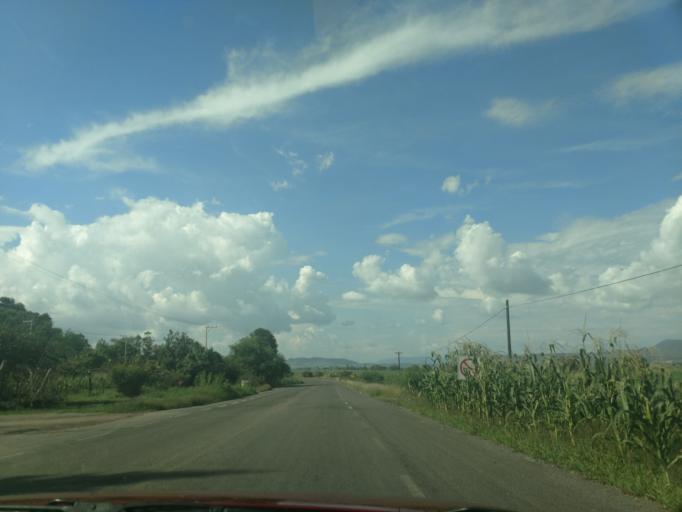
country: MX
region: Jalisco
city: Antonio Escobedo
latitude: 20.8506
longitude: -104.0285
